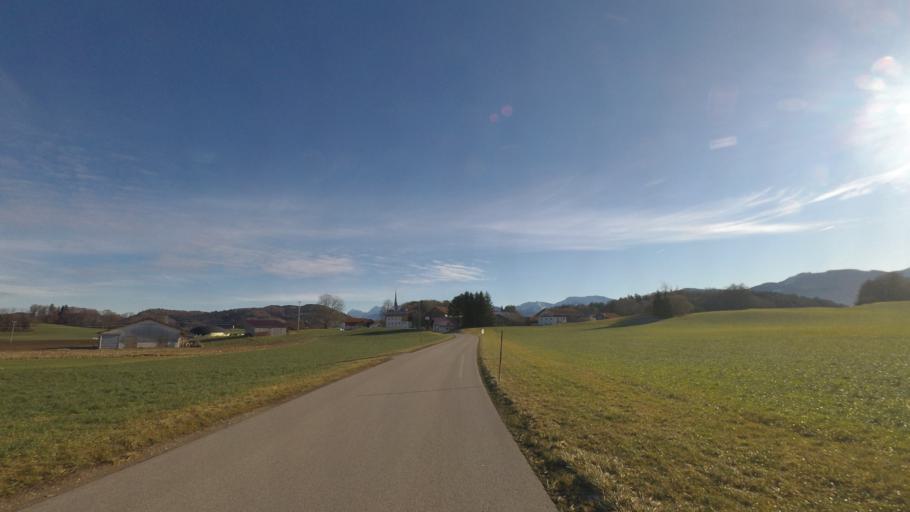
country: DE
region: Bavaria
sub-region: Upper Bavaria
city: Bergen
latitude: 47.8378
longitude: 12.5824
